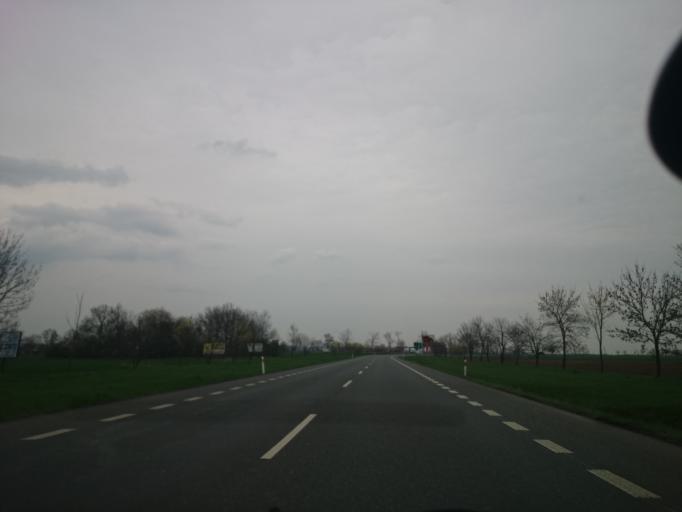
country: PL
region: Opole Voivodeship
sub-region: Powiat nyski
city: Paczkow
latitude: 50.4572
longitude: 17.0231
